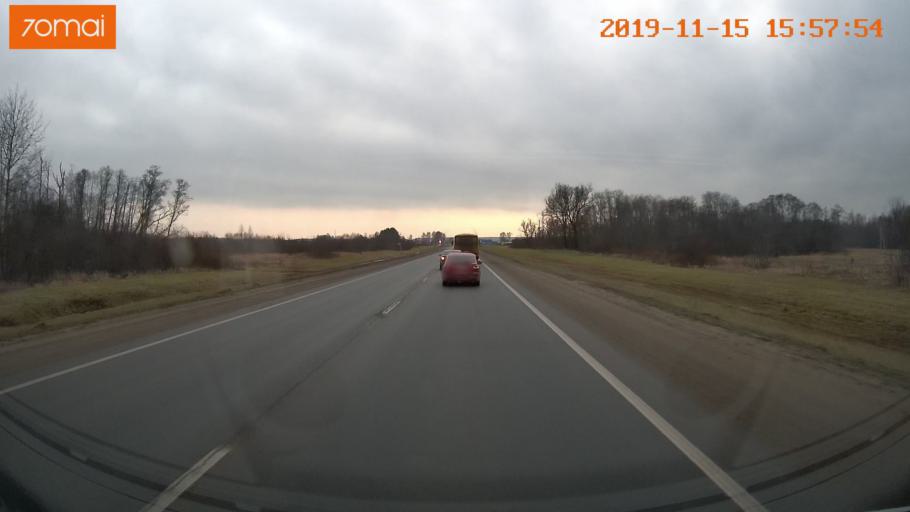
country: RU
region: Jaroslavl
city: Yaroslavl
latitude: 57.8257
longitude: 39.9595
